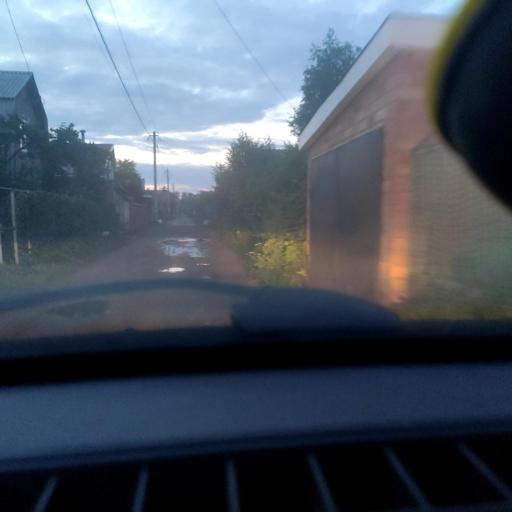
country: RU
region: Samara
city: Tol'yatti
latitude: 53.5941
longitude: 49.3146
